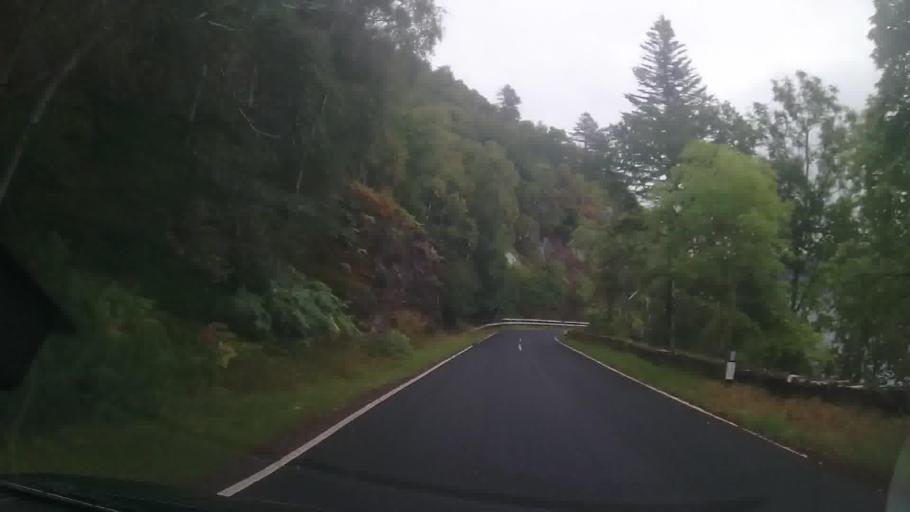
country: GB
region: Scotland
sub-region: Argyll and Bute
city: Isle Of Mull
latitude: 56.6775
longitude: -5.8772
